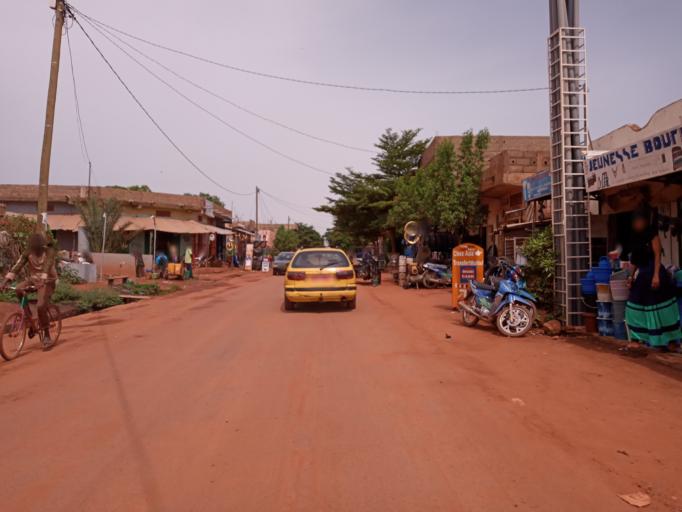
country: ML
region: Bamako
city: Bamako
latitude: 12.5536
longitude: -7.9953
